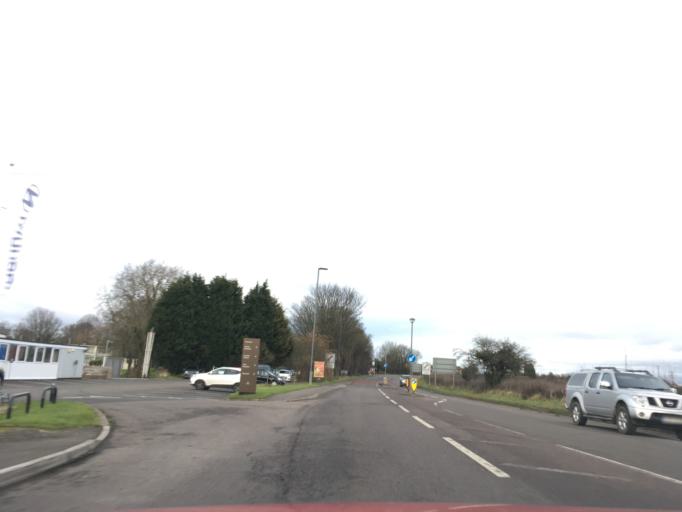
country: GB
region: England
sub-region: South Gloucestershire
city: Alveston
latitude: 51.5909
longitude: -2.5267
